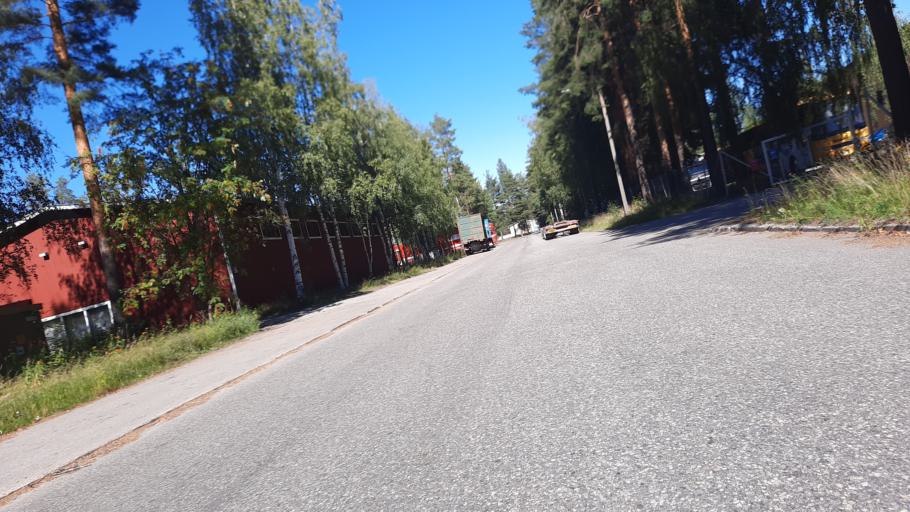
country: FI
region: North Karelia
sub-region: Joensuu
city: Joensuu
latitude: 62.6219
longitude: 29.7495
